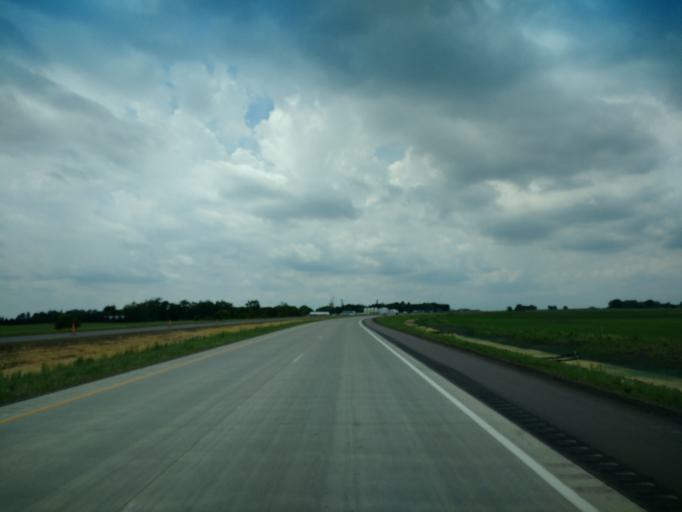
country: US
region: Minnesota
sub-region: Cottonwood County
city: Windom
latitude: 43.9113
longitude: -95.0274
